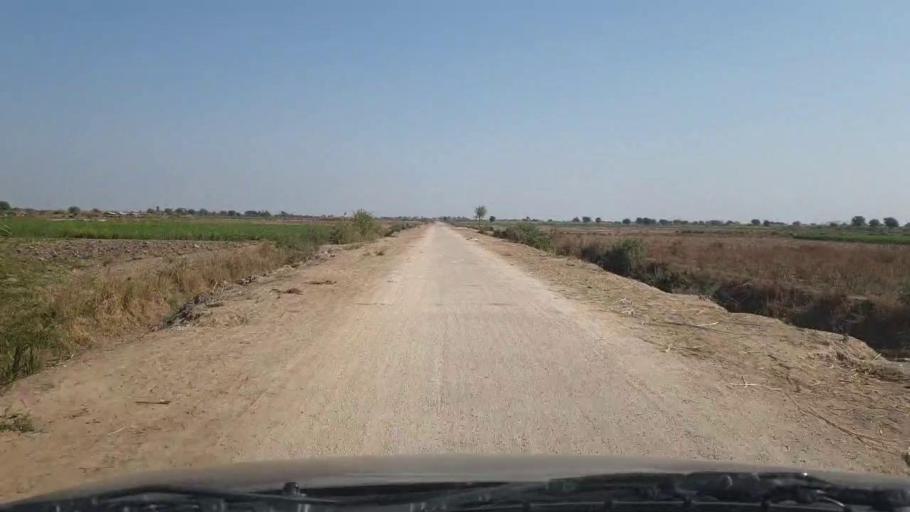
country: PK
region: Sindh
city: Samaro
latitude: 25.1990
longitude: 69.2918
